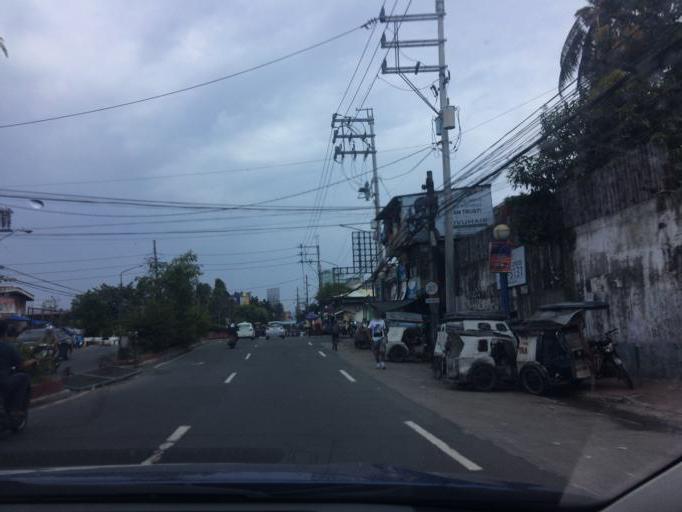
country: PH
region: Metro Manila
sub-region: Makati City
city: Makati City
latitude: 14.5313
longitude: 121.0043
